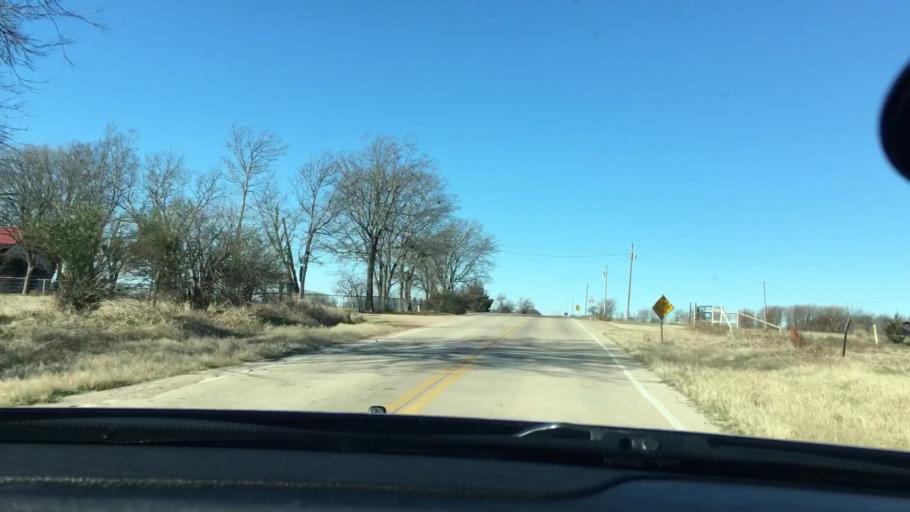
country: US
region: Oklahoma
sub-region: Marshall County
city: Madill
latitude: 34.1145
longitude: -96.6532
